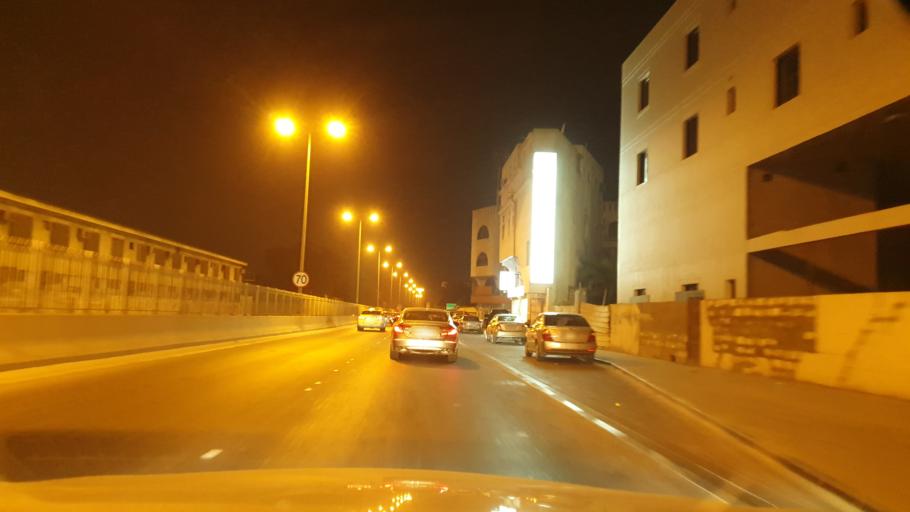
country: BH
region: Manama
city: Jidd Hafs
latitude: 26.2161
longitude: 50.5331
